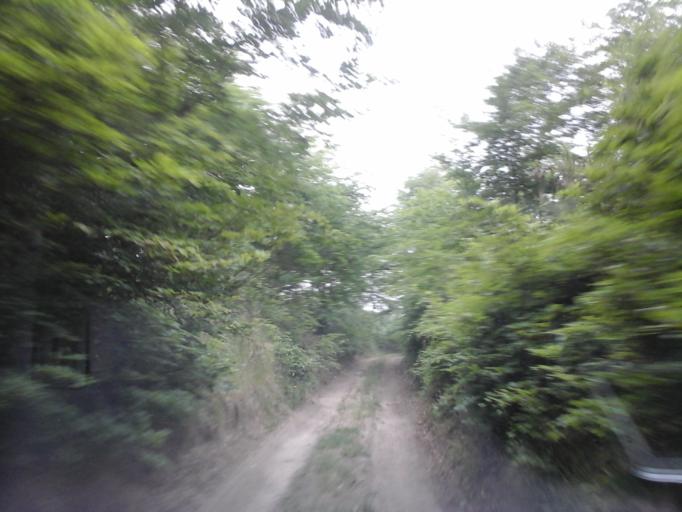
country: PL
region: West Pomeranian Voivodeship
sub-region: Powiat choszczenski
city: Pelczyce
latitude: 52.9651
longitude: 15.3735
